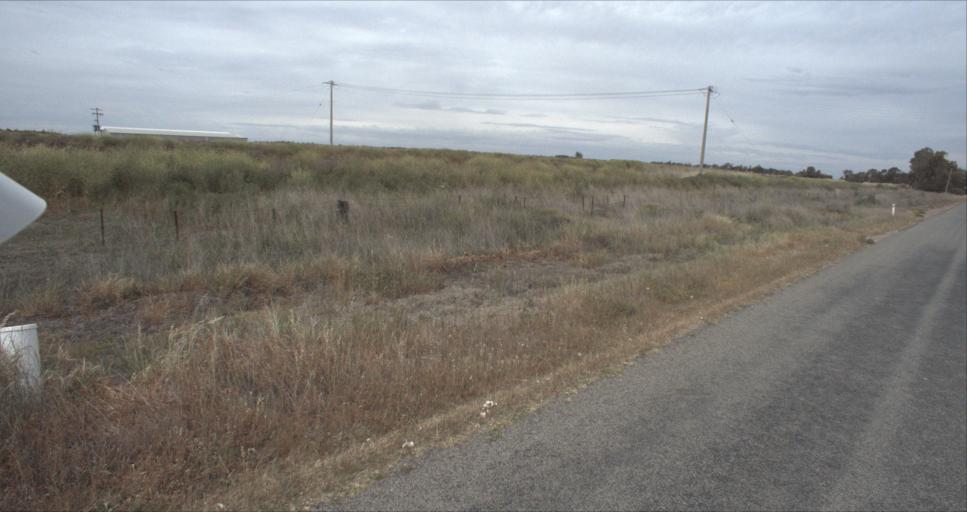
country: AU
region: New South Wales
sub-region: Leeton
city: Leeton
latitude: -34.4382
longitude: 146.3761
